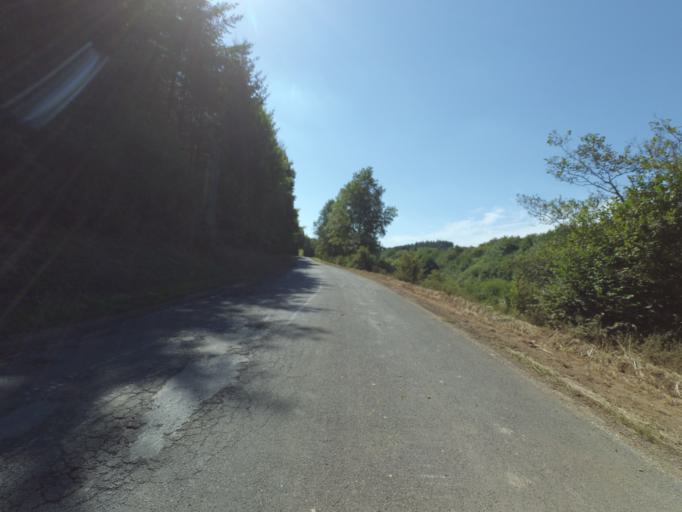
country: DE
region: Rheinland-Pfalz
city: Steiningen
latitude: 50.1866
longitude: 6.9080
